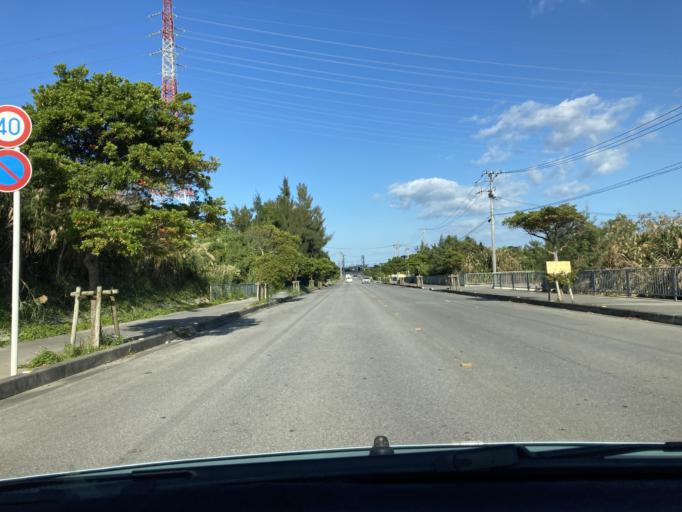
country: JP
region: Okinawa
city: Gushikawa
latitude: 26.3786
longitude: 127.8347
